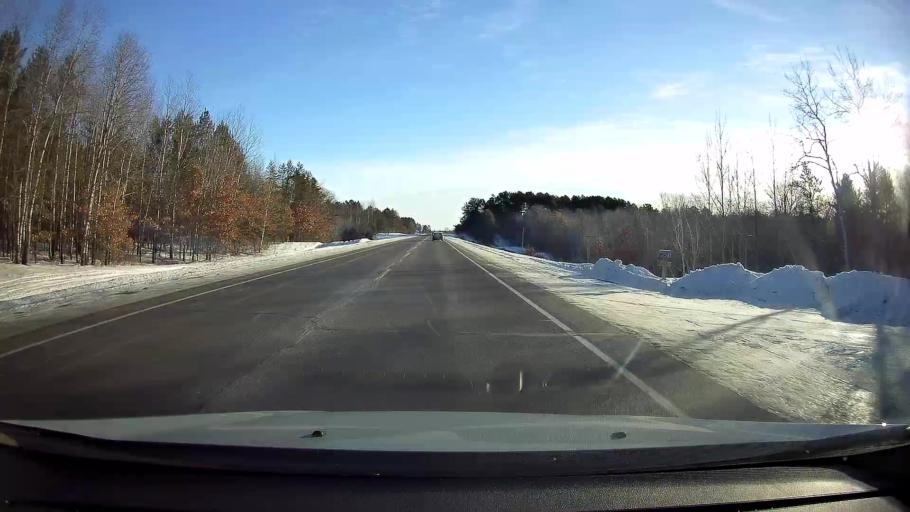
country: US
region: Wisconsin
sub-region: Washburn County
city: Spooner
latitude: 45.9104
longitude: -91.7775
